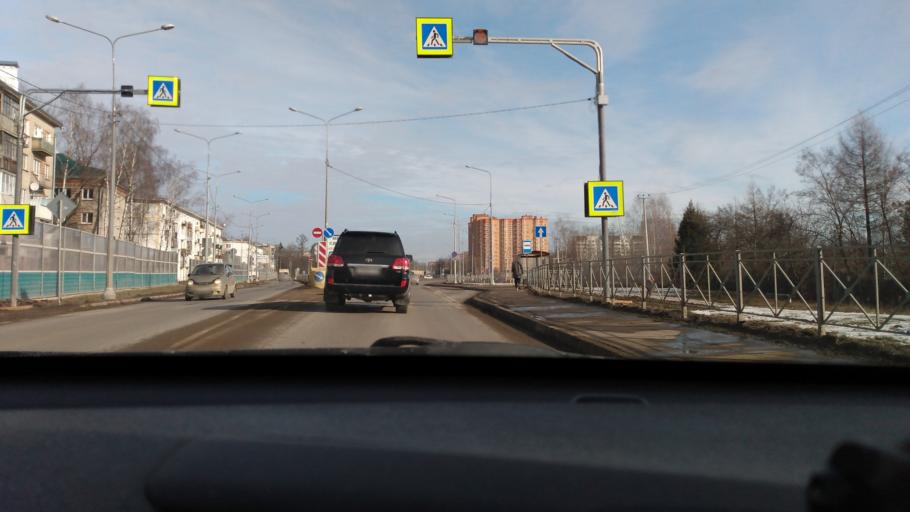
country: RU
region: Moskovskaya
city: Nakhabino
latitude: 55.8360
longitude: 37.1569
